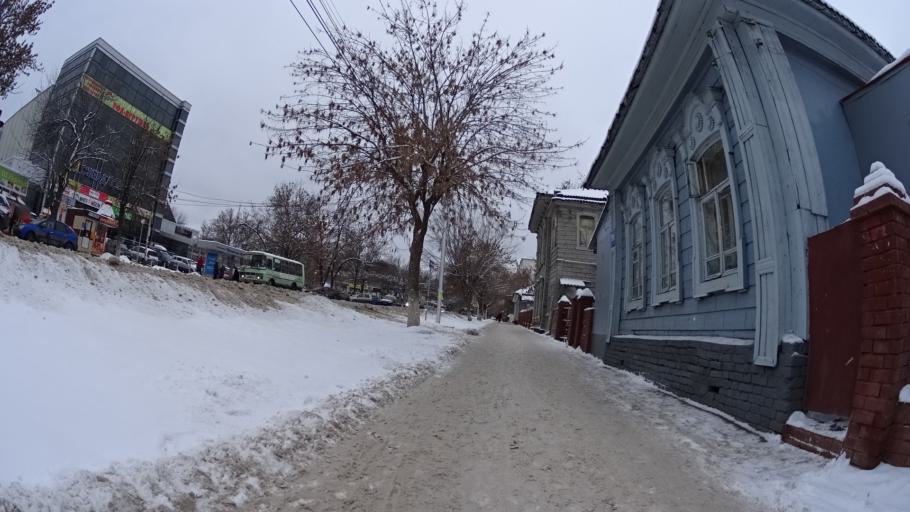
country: RU
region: Bashkortostan
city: Ufa
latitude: 54.7259
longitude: 55.9391
